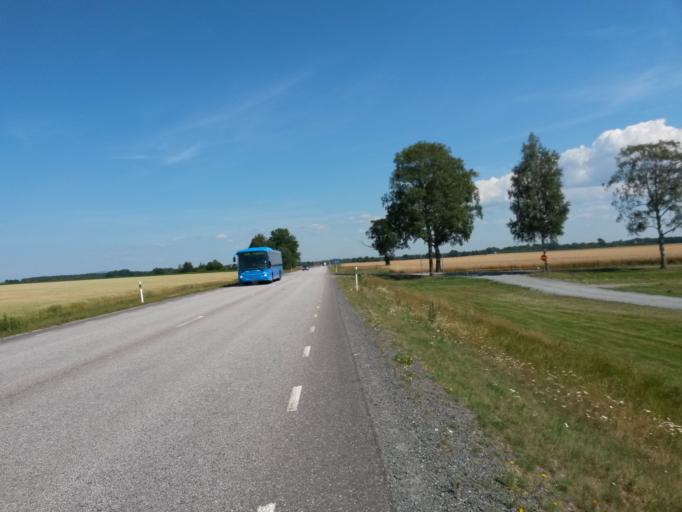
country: SE
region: Vaestra Goetaland
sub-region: Lidkopings Kommun
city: Lidkoping
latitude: 58.4802
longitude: 13.0936
